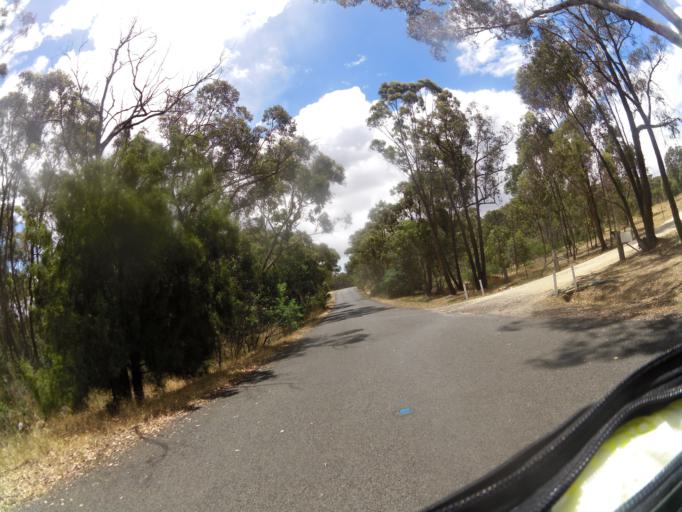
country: AU
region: Victoria
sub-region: Mount Alexander
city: Castlemaine
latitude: -37.0233
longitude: 144.2421
